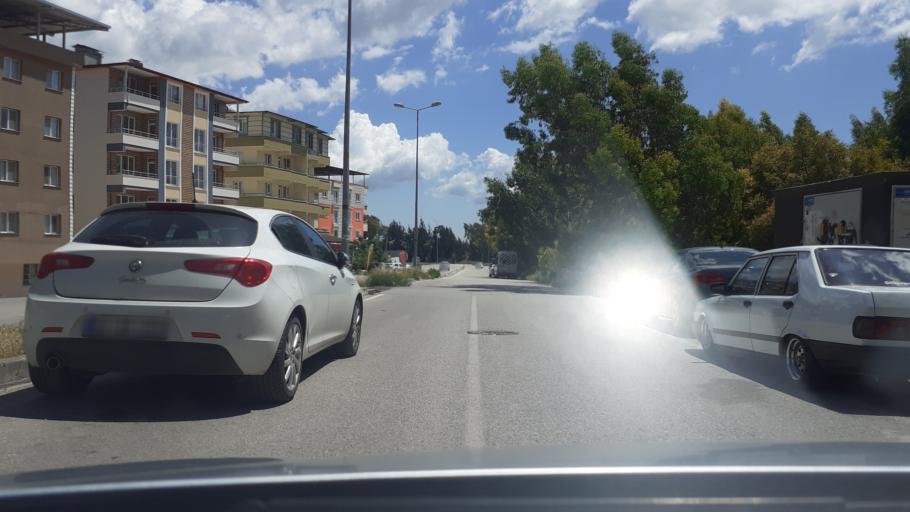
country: TR
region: Hatay
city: Anayazi
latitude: 36.3347
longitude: 36.2034
